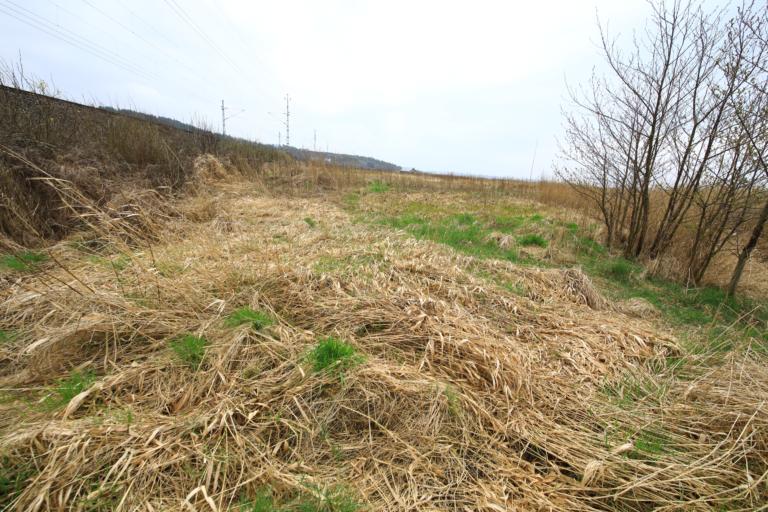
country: SE
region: Halland
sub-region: Kungsbacka Kommun
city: Frillesas
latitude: 57.3111
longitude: 12.1706
